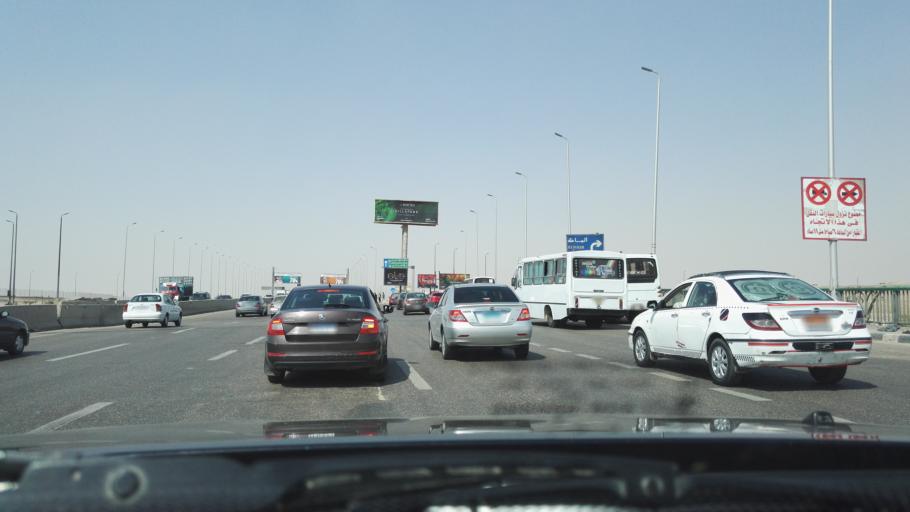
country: EG
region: Muhafazat al Qalyubiyah
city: Al Khankah
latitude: 30.0800
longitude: 31.4357
